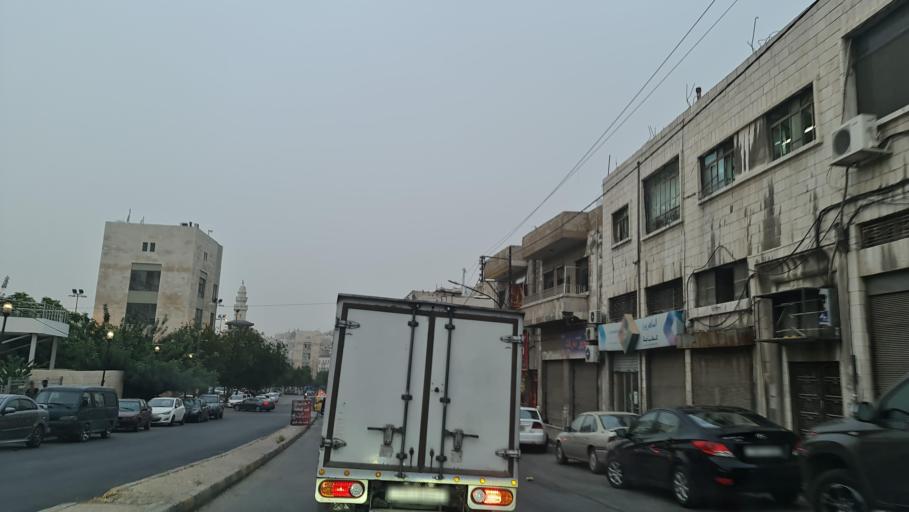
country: JO
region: Amman
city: Amman
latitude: 31.9520
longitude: 35.9408
